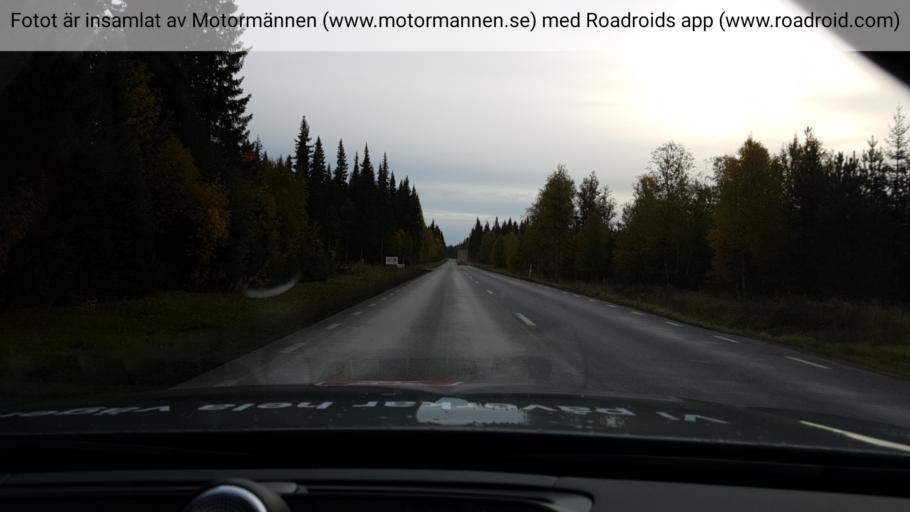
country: SE
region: Jaemtland
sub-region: Stroemsunds Kommun
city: Stroemsund
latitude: 63.5199
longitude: 15.3008
